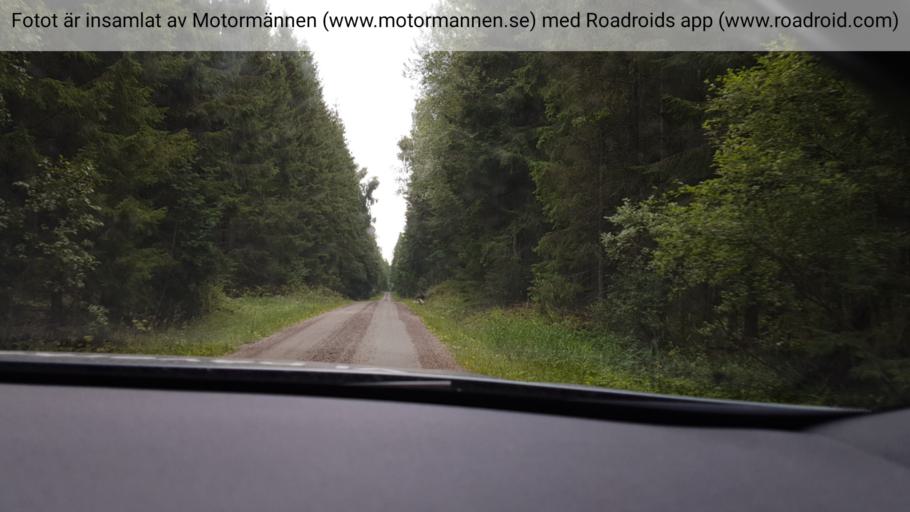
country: SE
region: Vaestra Goetaland
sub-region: Falkopings Kommun
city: Floby
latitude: 57.9822
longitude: 13.3391
